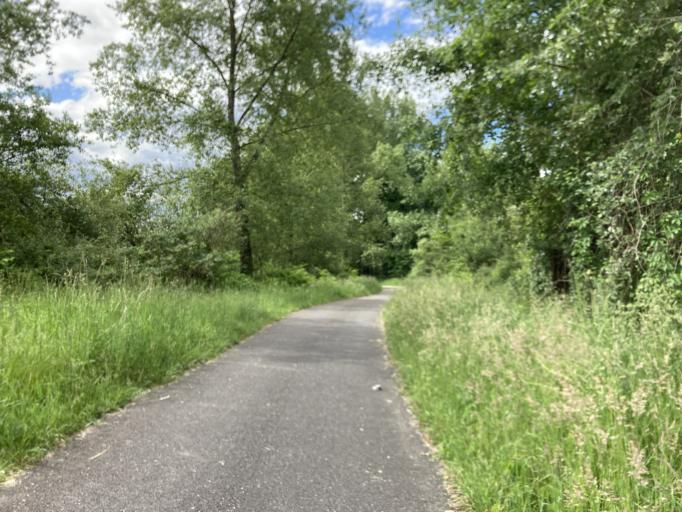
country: FR
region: Aquitaine
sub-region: Departement des Pyrenees-Atlantiques
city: Artiguelouve
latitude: 43.3167
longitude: -0.4518
